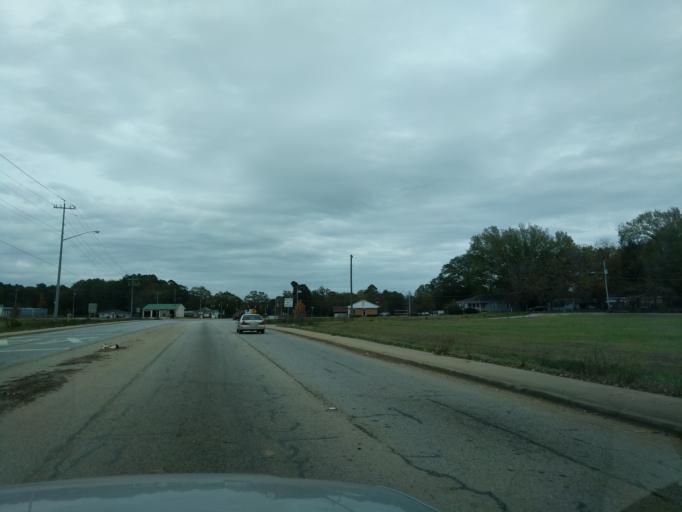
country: US
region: South Carolina
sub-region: Newberry County
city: Newberry
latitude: 34.2957
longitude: -81.6243
